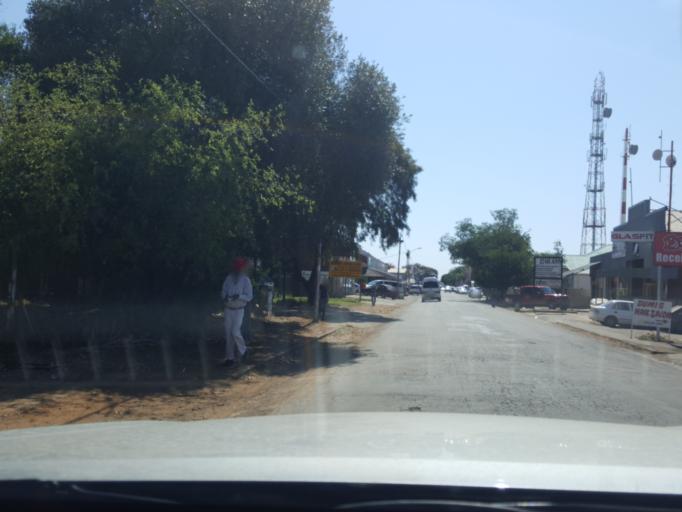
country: ZA
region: North-West
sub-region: Ngaka Modiri Molema District Municipality
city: Zeerust
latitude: -25.5449
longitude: 26.0758
